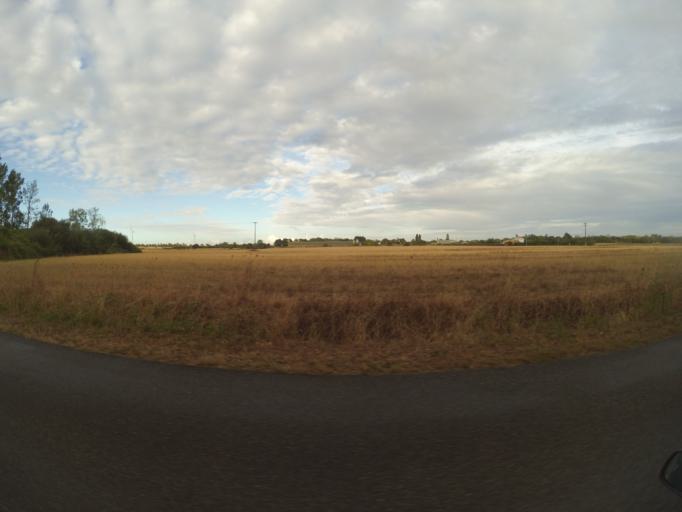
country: FR
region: Pays de la Loire
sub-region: Departement de la Loire-Atlantique
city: La Planche
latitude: 47.0102
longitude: -1.4560
